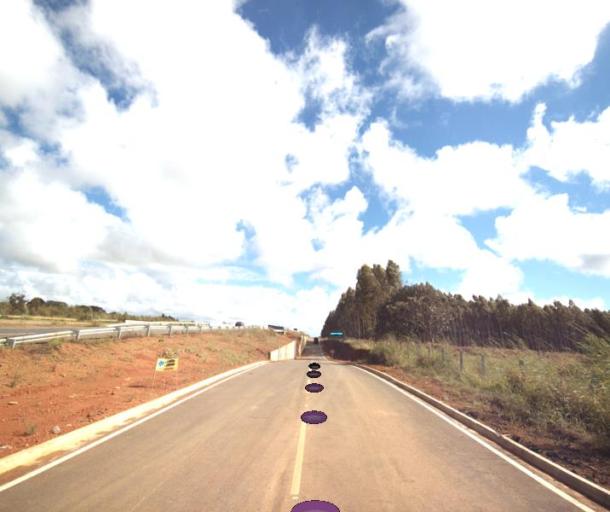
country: BR
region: Goias
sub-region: Anapolis
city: Anapolis
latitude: -16.2376
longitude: -49.0051
